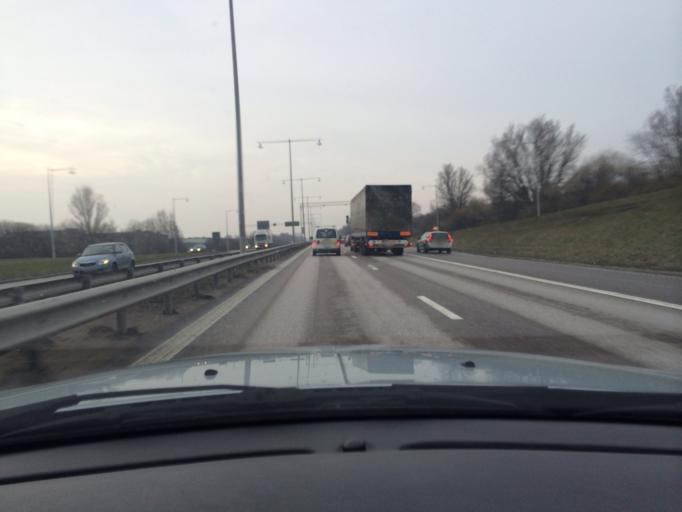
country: SE
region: Vaestra Goetaland
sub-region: Goteborg
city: Goeteborg
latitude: 57.7468
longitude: 11.9897
